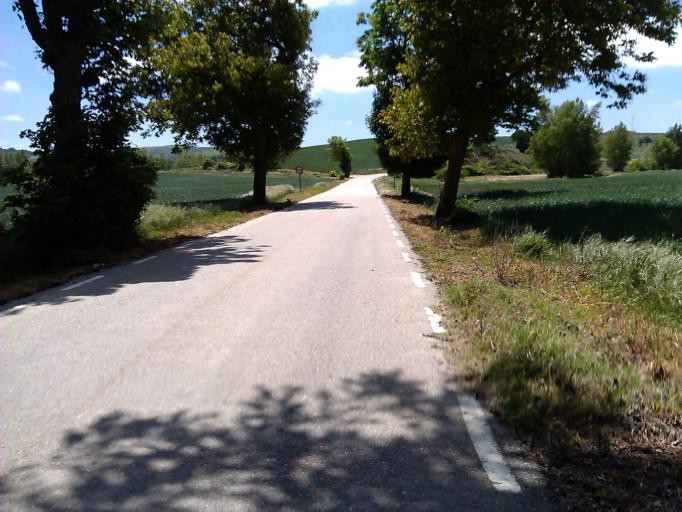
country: ES
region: Castille and Leon
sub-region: Provincia de Burgos
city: Cerraton de Juarros
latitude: 42.4370
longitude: -3.3525
